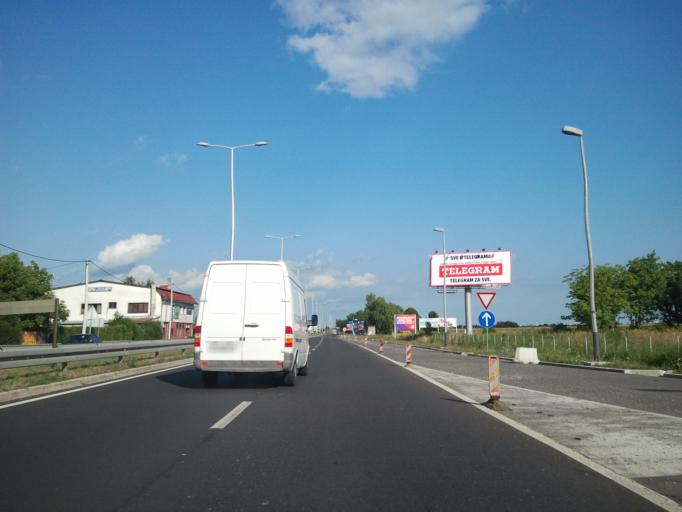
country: HR
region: Grad Zagreb
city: Odra
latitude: 45.7324
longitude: 16.0171
